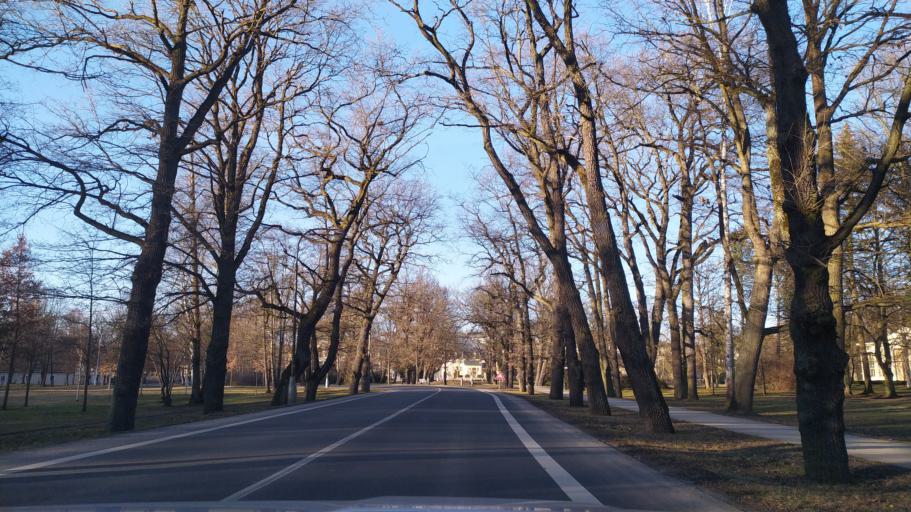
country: CZ
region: Karlovarsky
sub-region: Okres Cheb
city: Frantiskovy Lazne
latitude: 50.1164
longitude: 12.3497
